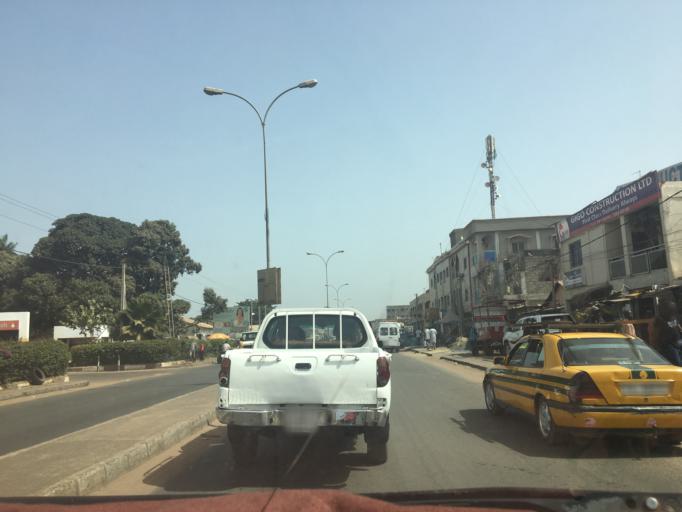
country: GM
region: Western
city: Abuko
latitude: 13.4327
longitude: -16.6755
